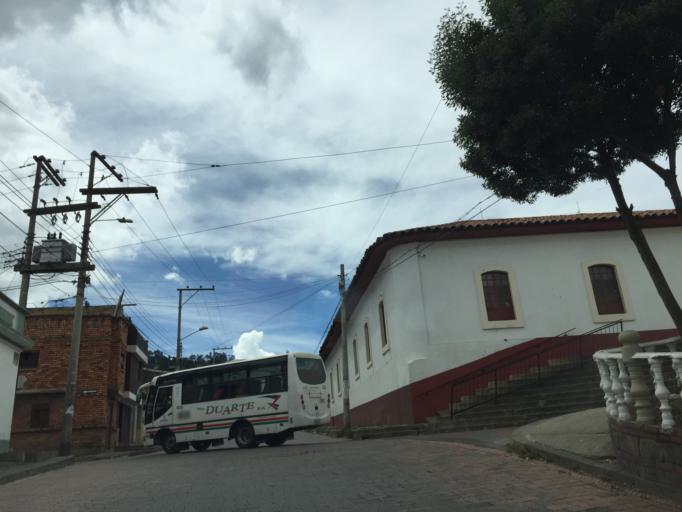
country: CO
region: Cundinamarca
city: Zipaquira
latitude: 5.0241
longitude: -74.0066
